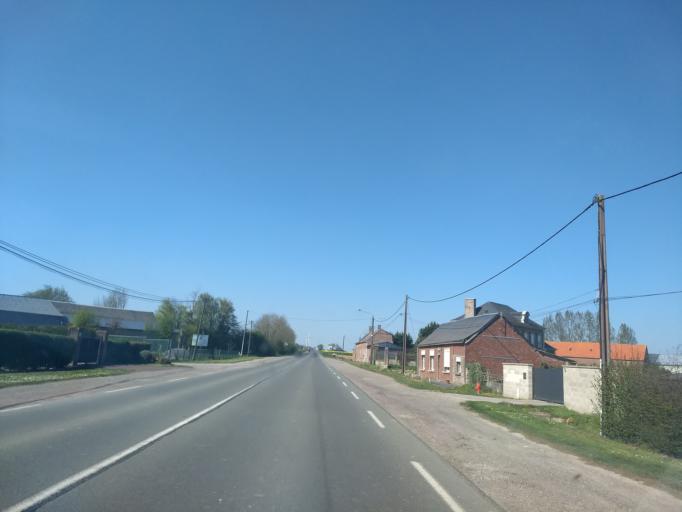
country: FR
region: Picardie
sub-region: Departement de la Somme
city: Talmas
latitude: 50.0587
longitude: 2.3235
